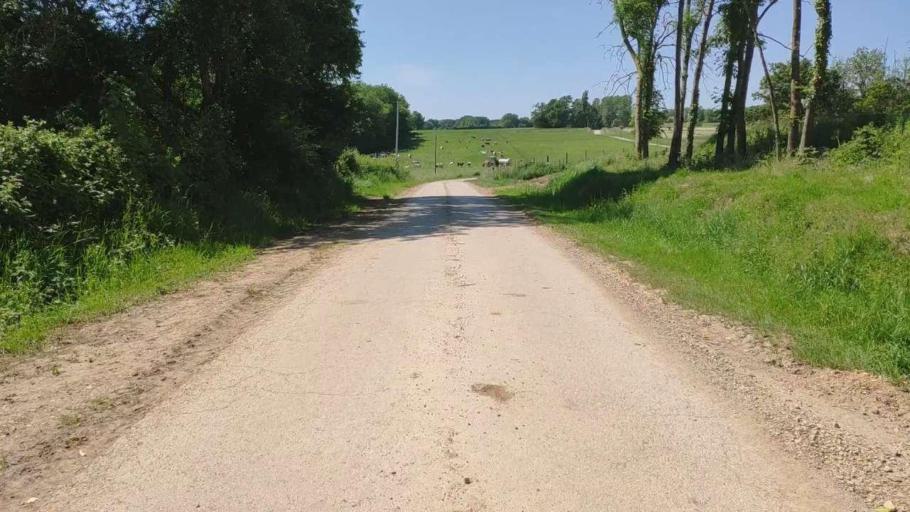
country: FR
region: Franche-Comte
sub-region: Departement du Jura
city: Bletterans
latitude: 46.7742
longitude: 5.3936
